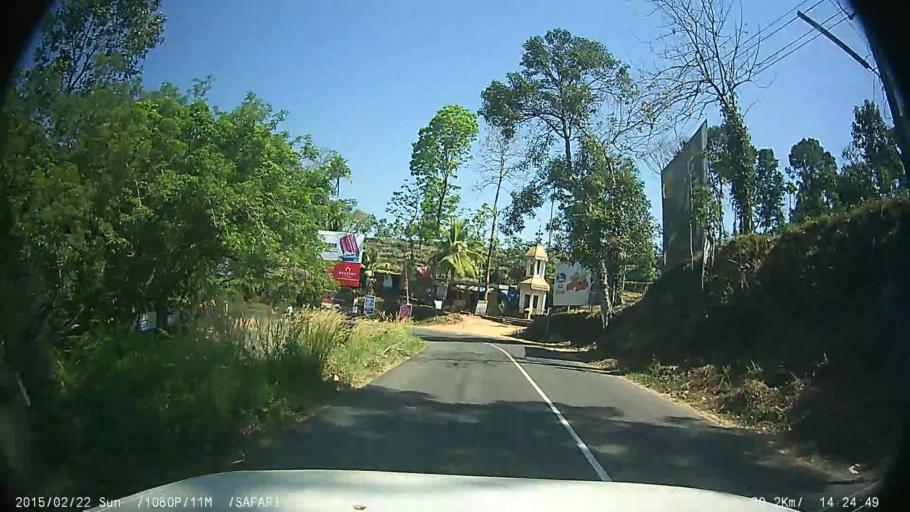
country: IN
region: Kerala
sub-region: Kottayam
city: Erattupetta
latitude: 9.5707
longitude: 76.7169
